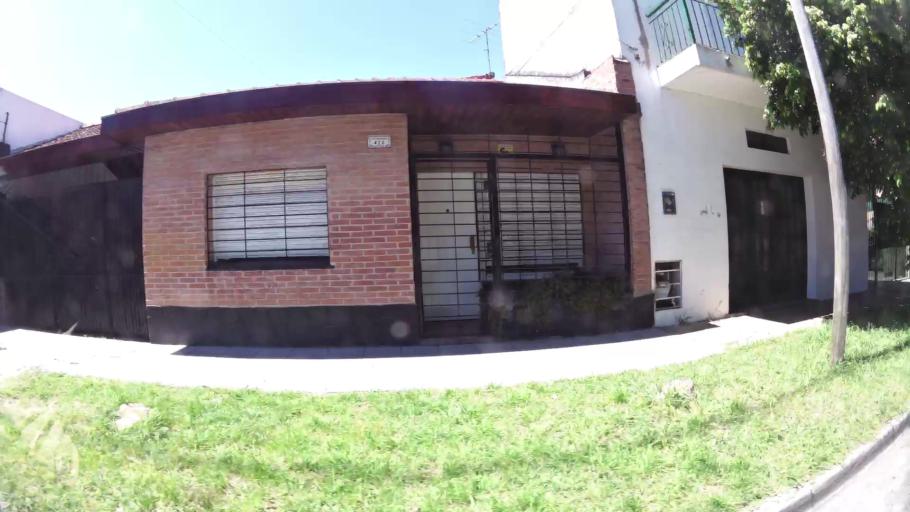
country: AR
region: Buenos Aires
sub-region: Partido de Vicente Lopez
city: Olivos
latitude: -34.5144
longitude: -58.5353
